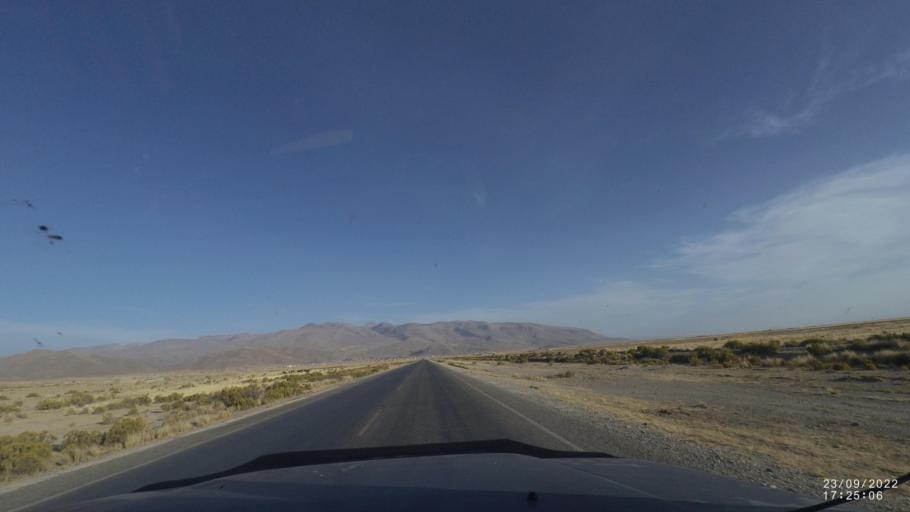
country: BO
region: Oruro
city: Challapata
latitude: -18.8657
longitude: -66.8013
